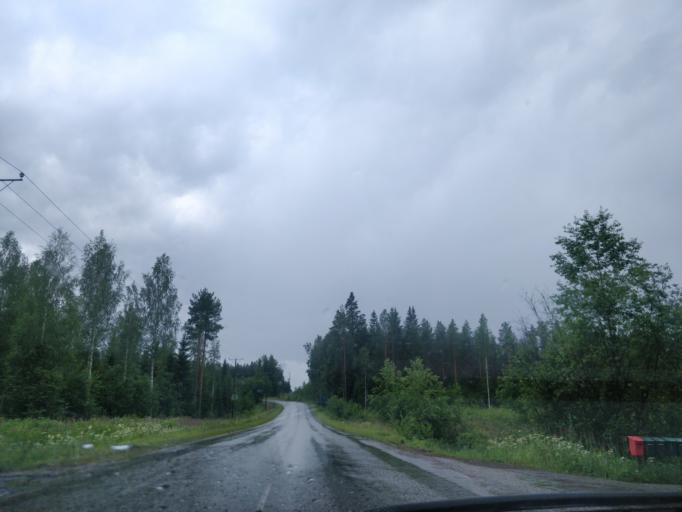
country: FI
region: Southern Savonia
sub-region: Mikkeli
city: Pertunmaa
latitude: 61.3864
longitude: 26.3103
